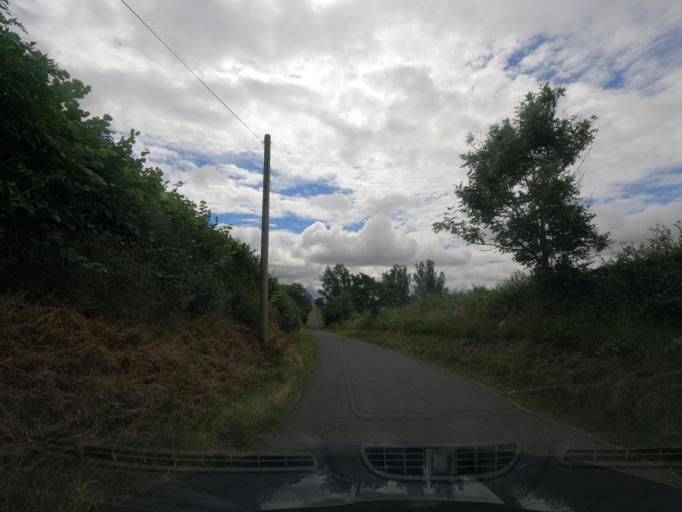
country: GB
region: Scotland
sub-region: The Scottish Borders
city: Allanton
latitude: 55.7289
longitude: -2.1973
